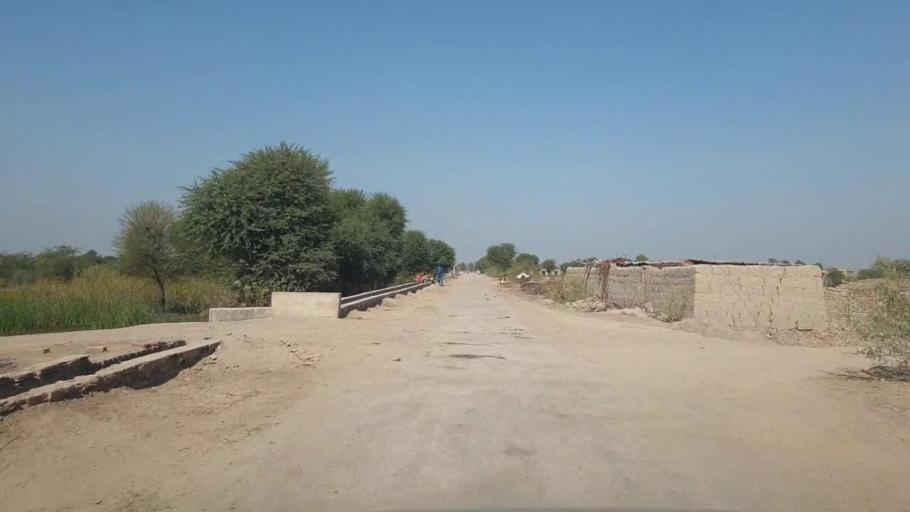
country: PK
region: Sindh
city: Chambar
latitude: 25.2906
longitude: 68.6918
